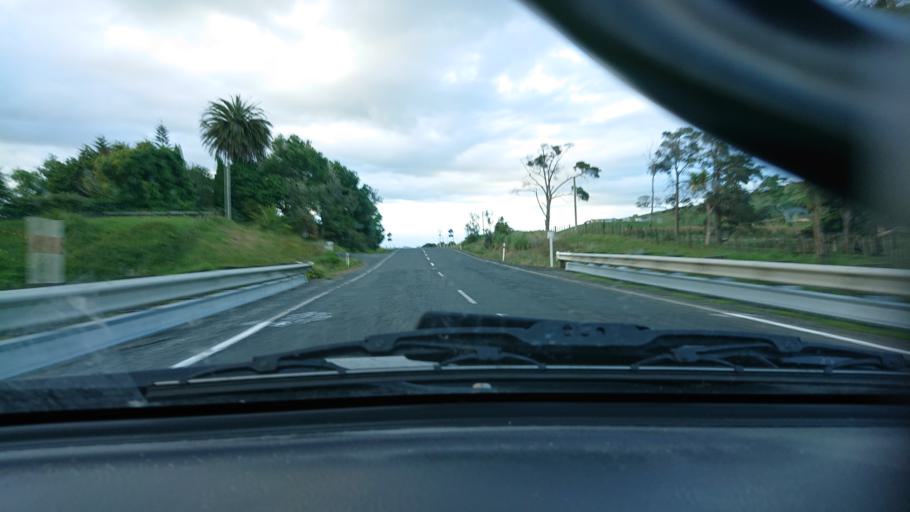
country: NZ
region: Auckland
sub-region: Auckland
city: Wellsford
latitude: -36.4546
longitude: 174.4357
